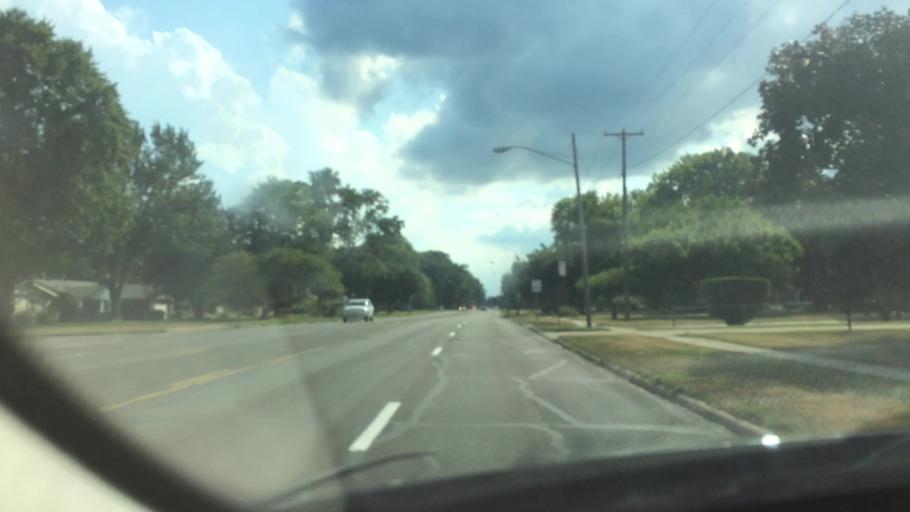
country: US
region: Ohio
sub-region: Wood County
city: Perrysburg
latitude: 41.6004
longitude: -83.6301
